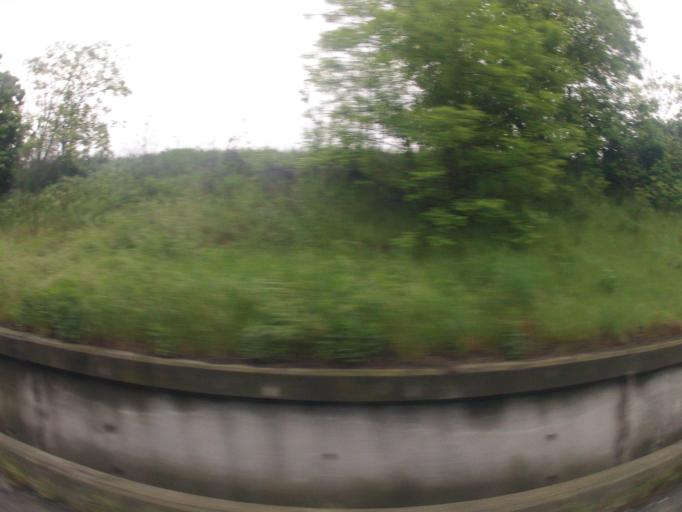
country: IT
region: Piedmont
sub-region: Provincia di Torino
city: La Loggia
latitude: 44.9502
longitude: 7.6792
